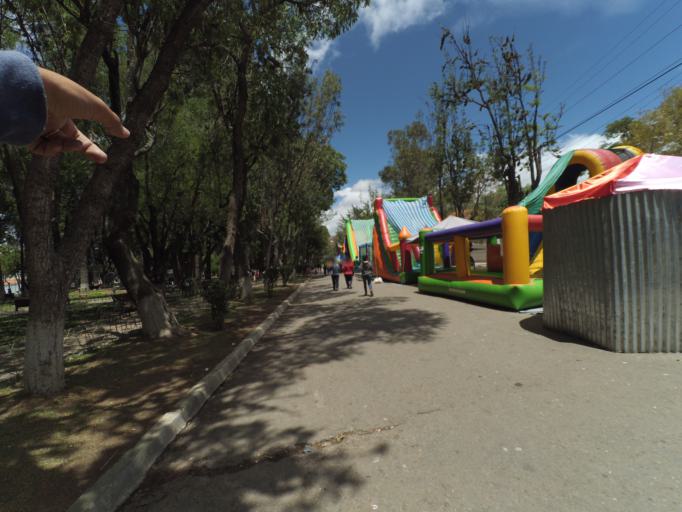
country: BO
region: Chuquisaca
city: Sucre
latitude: -19.0422
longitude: -65.2634
